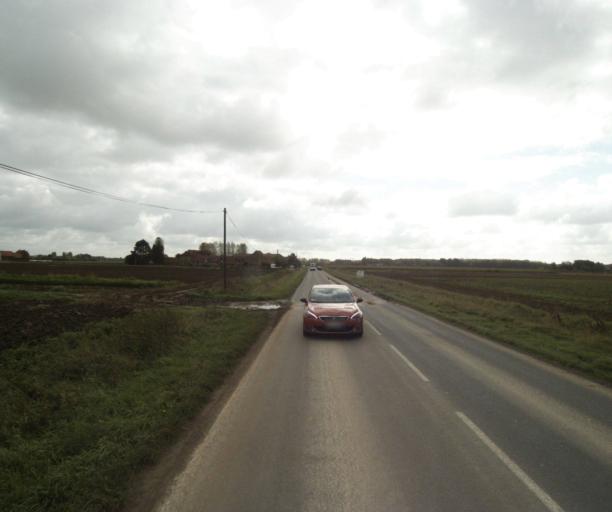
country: FR
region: Nord-Pas-de-Calais
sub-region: Departement du Nord
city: Verlinghem
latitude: 50.6947
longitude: 2.9805
